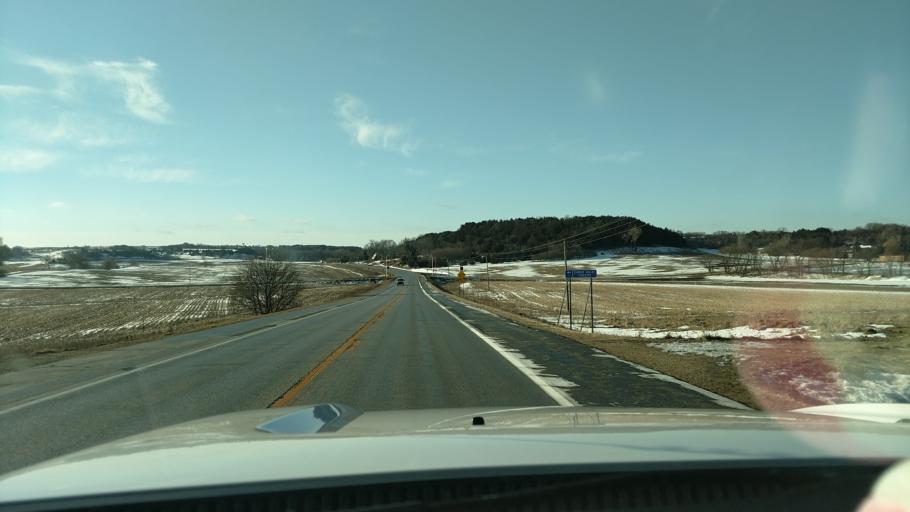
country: US
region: Minnesota
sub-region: Olmsted County
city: Oronoco
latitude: 44.1401
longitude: -92.4159
